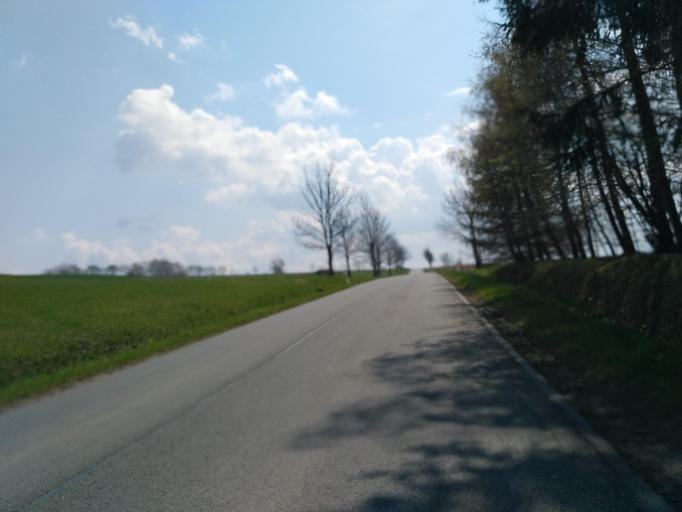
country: PL
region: Subcarpathian Voivodeship
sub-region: Powiat sanocki
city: Bukowsko
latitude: 49.4983
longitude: 22.0398
